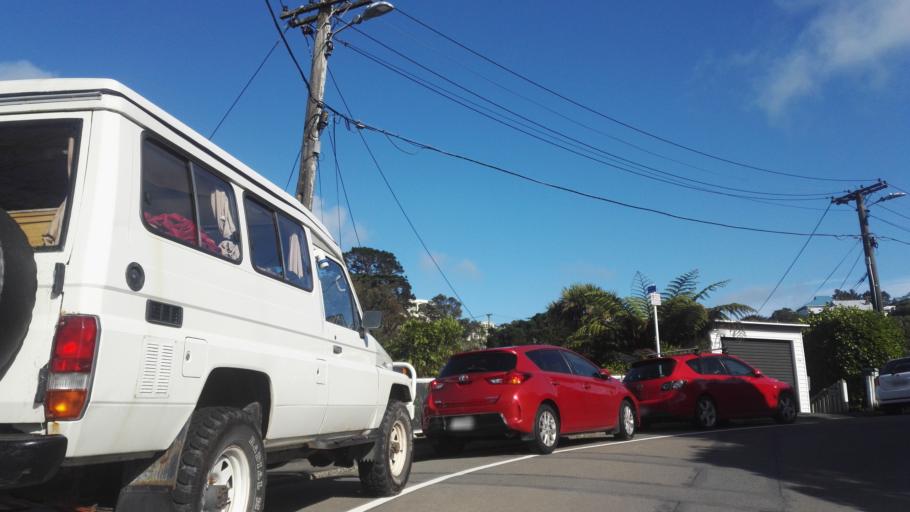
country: NZ
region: Wellington
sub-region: Wellington City
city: Kelburn
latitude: -41.2924
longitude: 174.7642
